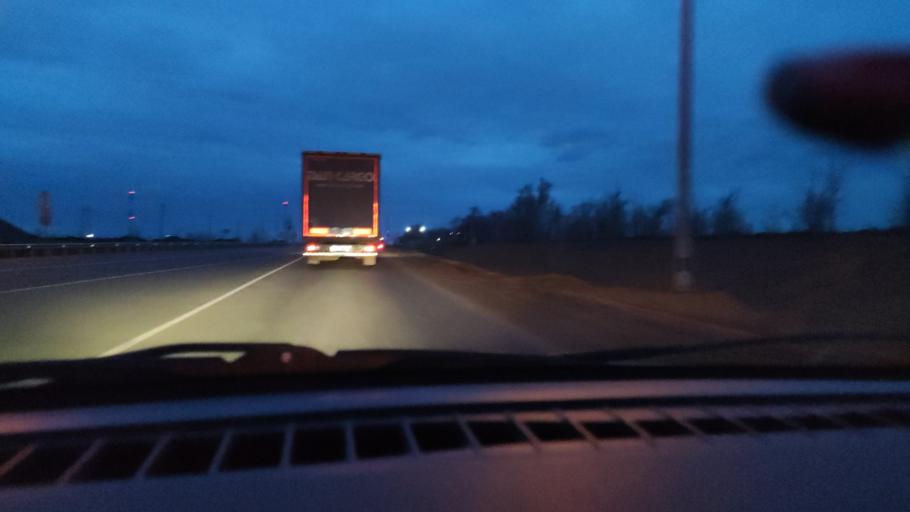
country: RU
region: Orenburg
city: Tatarskaya Kargala
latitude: 51.9709
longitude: 55.1858
